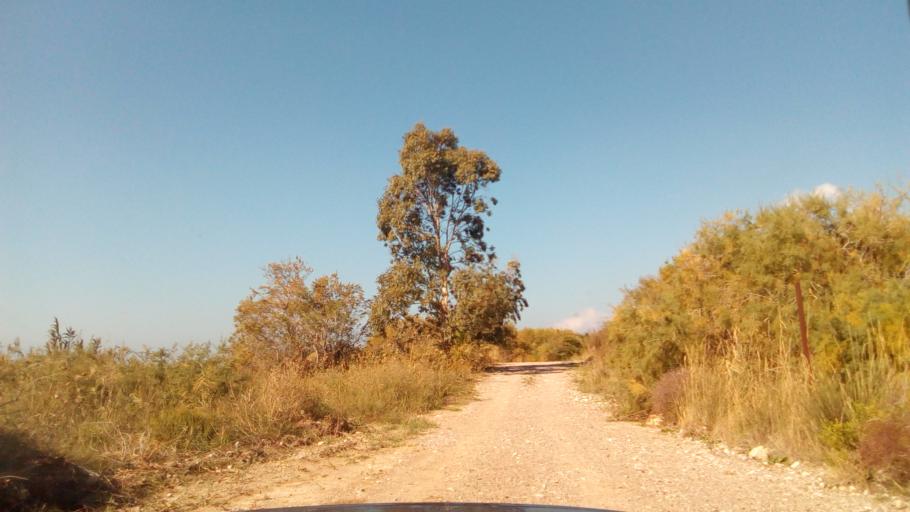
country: GR
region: West Greece
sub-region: Nomos Aitolias kai Akarnanias
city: Antirrio
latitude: 38.3317
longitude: 21.7519
